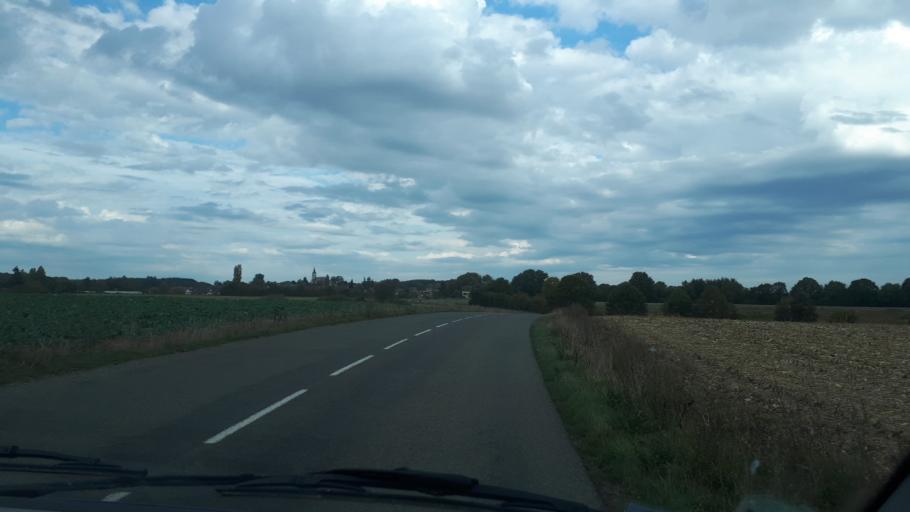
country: FR
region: Centre
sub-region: Departement d'Eure-et-Loir
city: Authon-du-Perche
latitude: 48.1881
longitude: 0.9081
